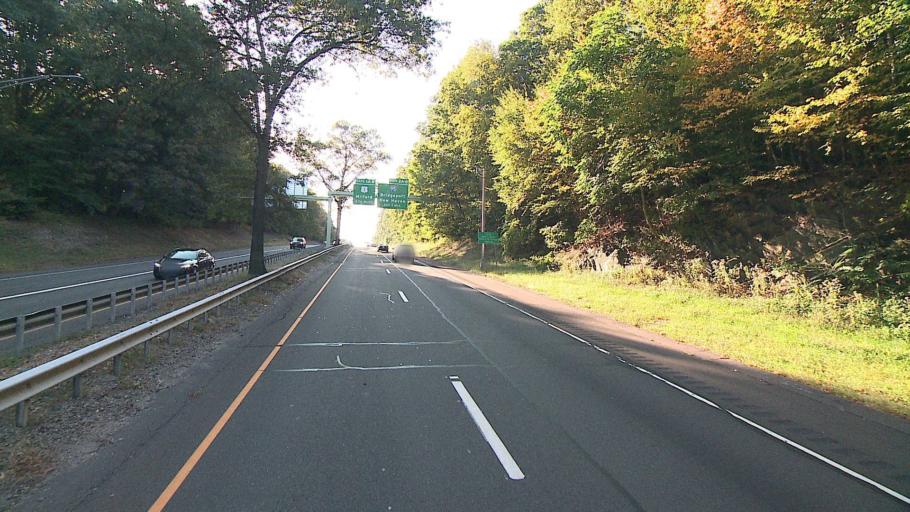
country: US
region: Connecticut
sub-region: New Haven County
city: City of Milford (balance)
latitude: 41.2446
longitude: -73.0828
